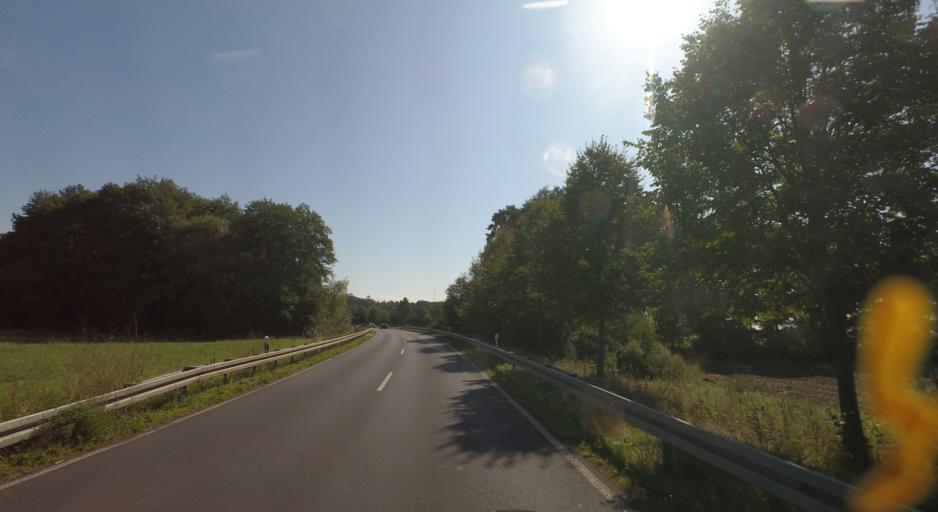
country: DE
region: Hesse
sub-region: Regierungsbezirk Darmstadt
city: Seligenstadt
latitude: 50.0290
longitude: 8.9796
